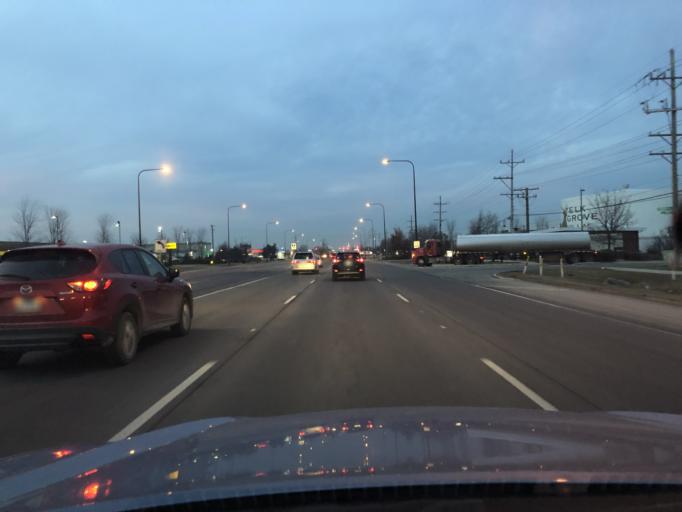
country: US
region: Illinois
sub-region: Cook County
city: Elk Grove Village
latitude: 42.0073
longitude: -87.9595
